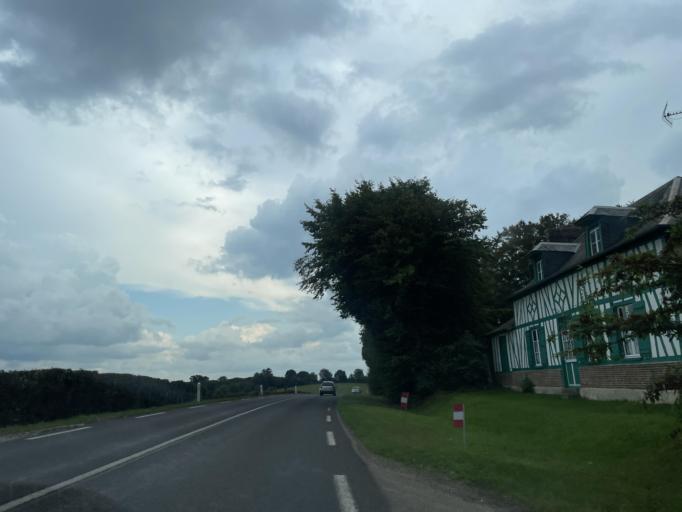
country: FR
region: Haute-Normandie
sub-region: Departement de la Seine-Maritime
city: Cayenne
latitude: 49.5903
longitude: 1.5942
